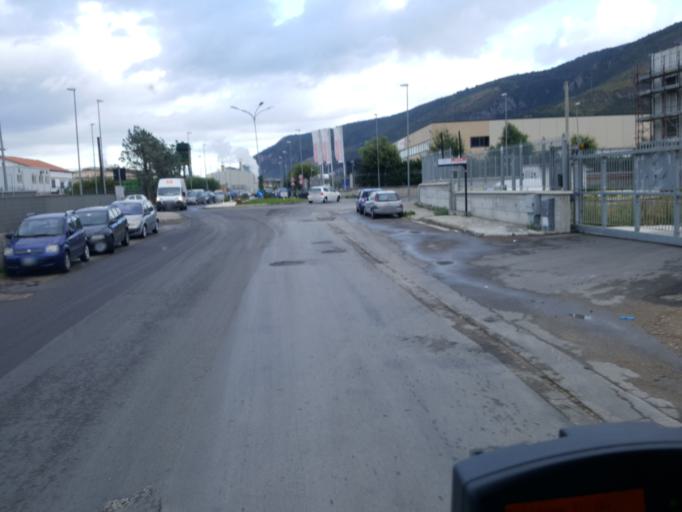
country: IT
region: Campania
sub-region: Provincia di Salerno
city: Sarno
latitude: 40.8198
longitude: 14.6018
